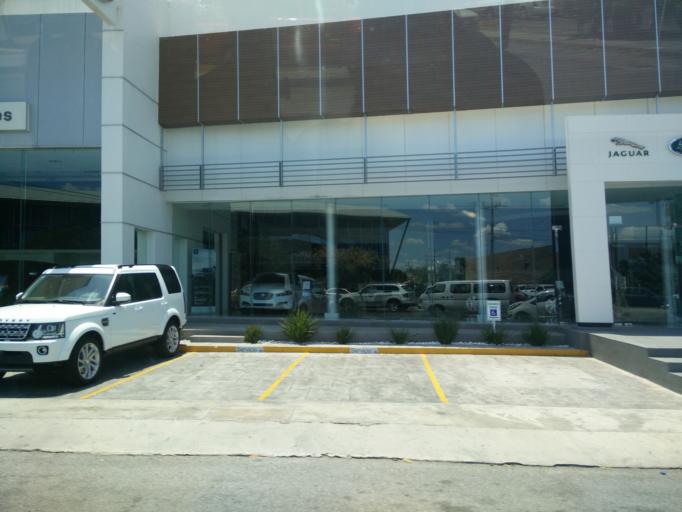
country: MX
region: Yucatan
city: Merida
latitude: 21.0241
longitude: -89.6227
